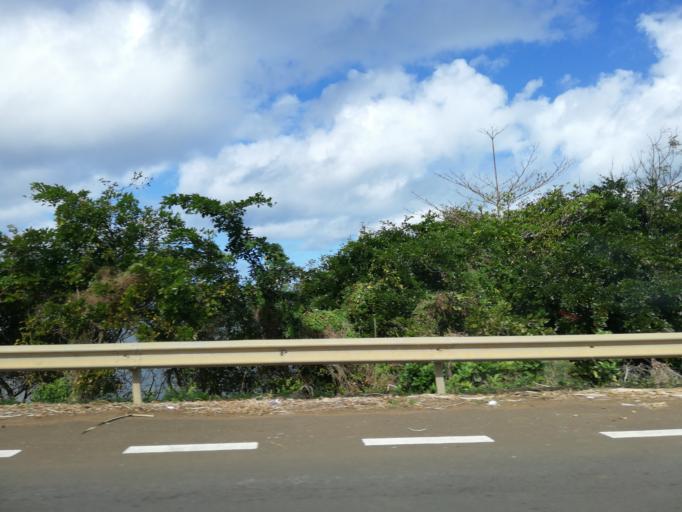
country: MU
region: Grand Port
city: Bois des Amourettes
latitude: -20.3702
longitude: 57.7015
